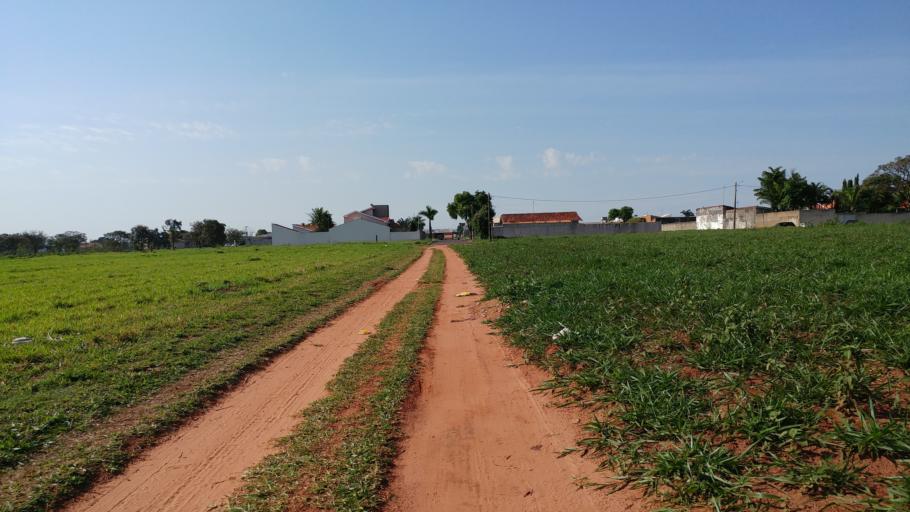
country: BR
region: Sao Paulo
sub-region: Paraguacu Paulista
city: Paraguacu Paulista
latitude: -22.4092
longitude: -50.5842
